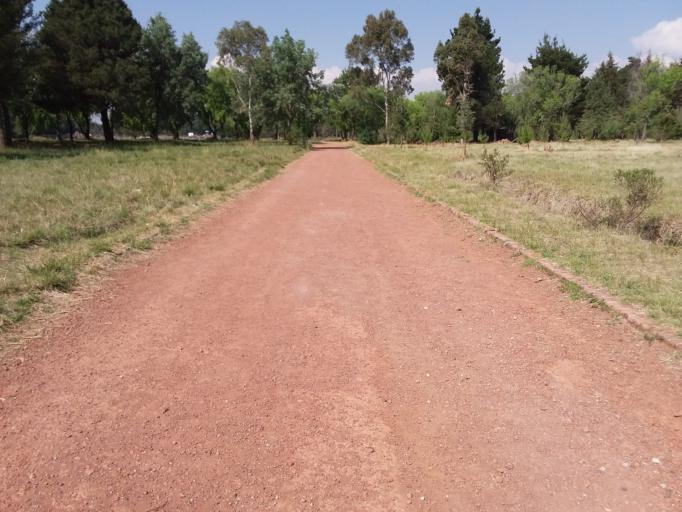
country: MX
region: Mexico
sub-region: Toluca
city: San Antonio Buenavista
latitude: 19.2726
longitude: -99.6963
